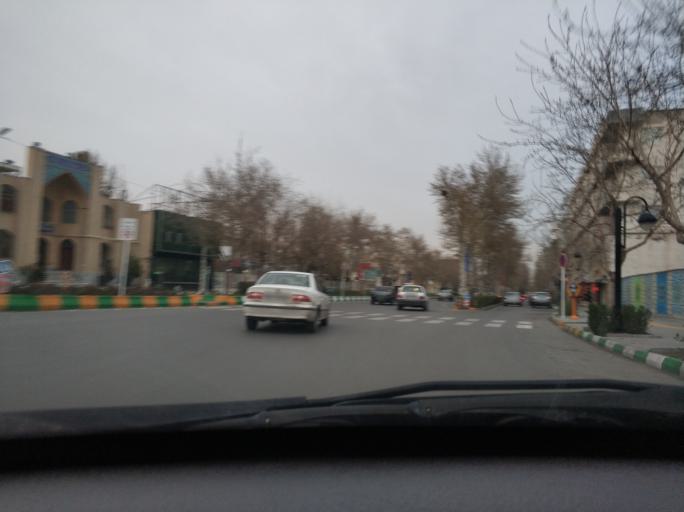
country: IR
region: Razavi Khorasan
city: Mashhad
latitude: 36.2753
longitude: 59.5924
